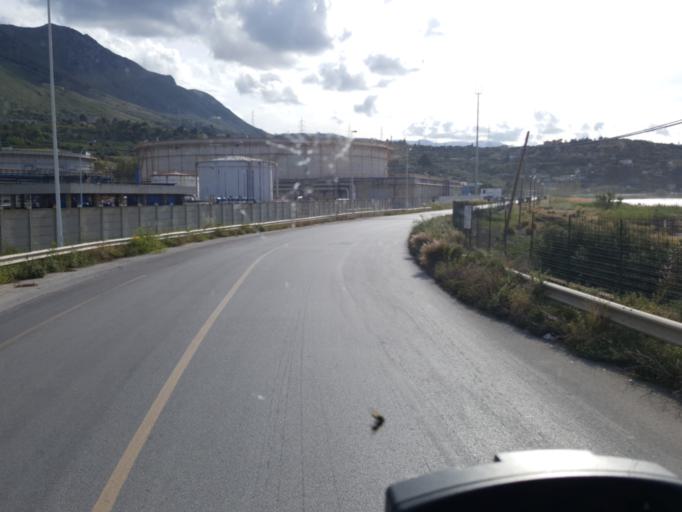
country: IT
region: Sicily
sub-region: Palermo
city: Termini Imerese
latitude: 37.9701
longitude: 13.7505
